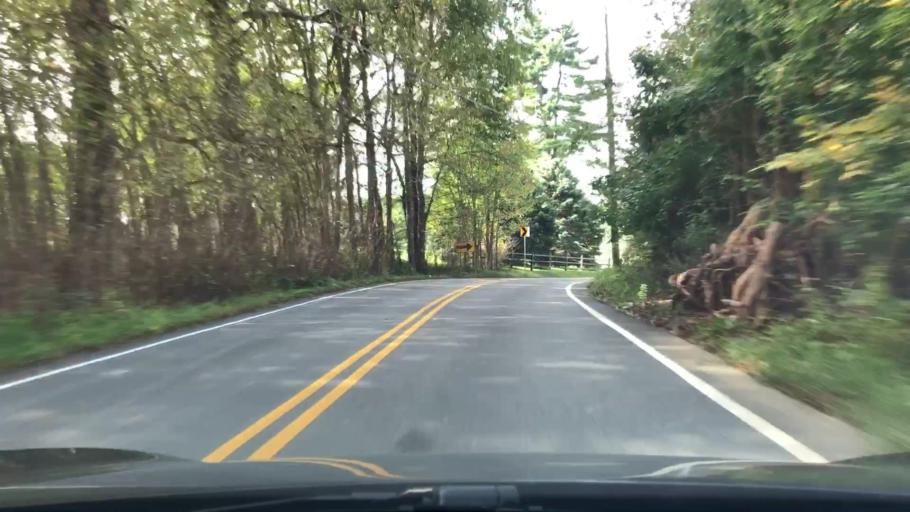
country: US
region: Pennsylvania
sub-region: Delaware County
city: Wayne
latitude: 40.0130
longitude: -75.3743
